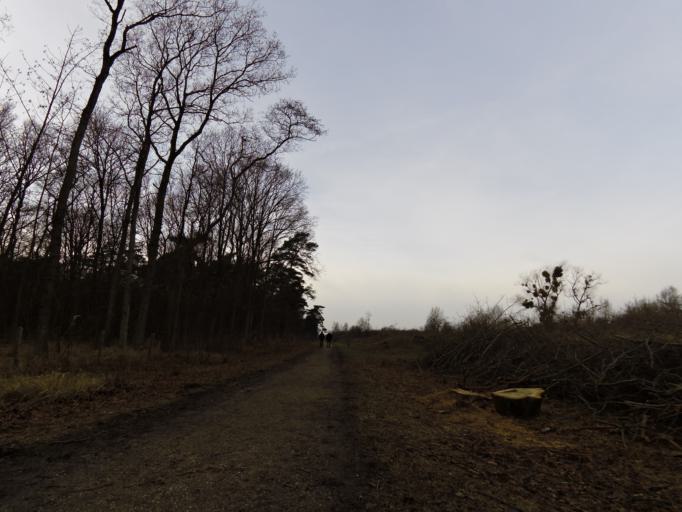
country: NL
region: South Holland
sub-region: Gemeente Hellevoetsluis
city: Nieuw-Helvoet
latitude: 51.9047
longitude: 4.0632
